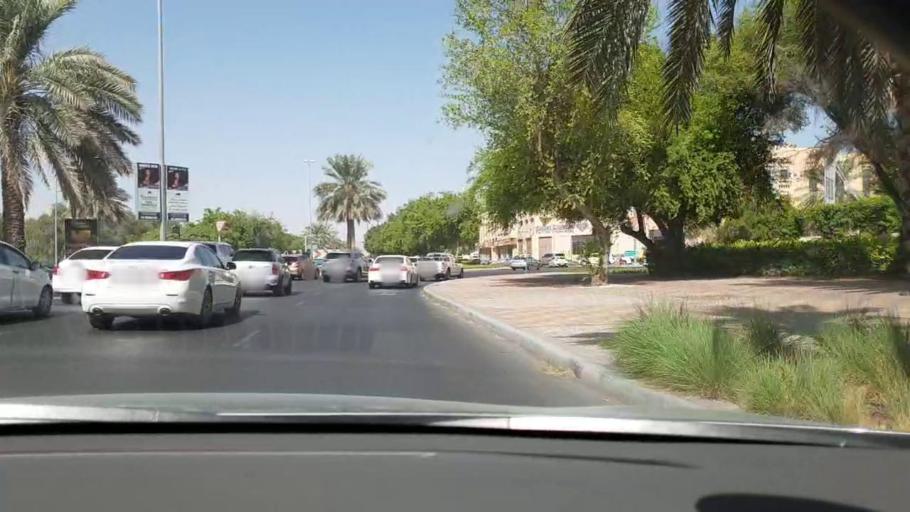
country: AE
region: Abu Dhabi
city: Al Ain
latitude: 24.2405
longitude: 55.7391
